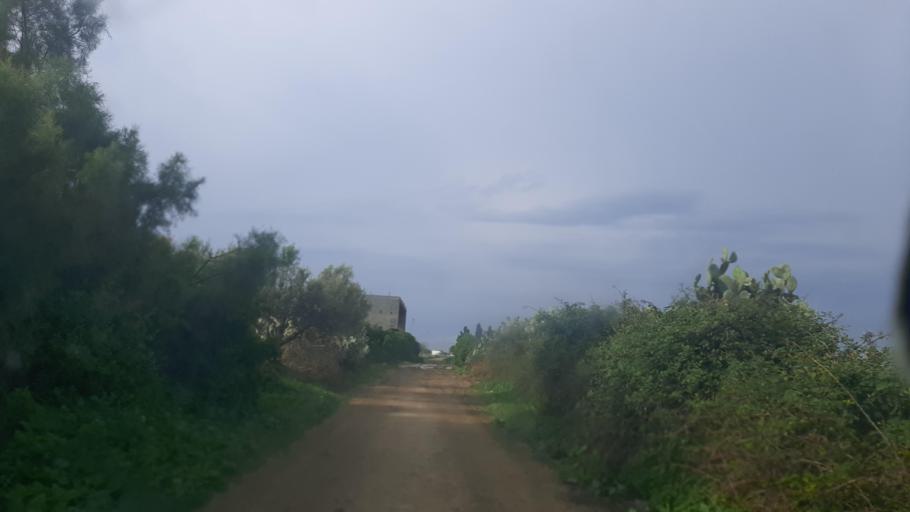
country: TN
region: Nabul
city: Menzel Heurr
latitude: 36.7899
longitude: 10.9600
